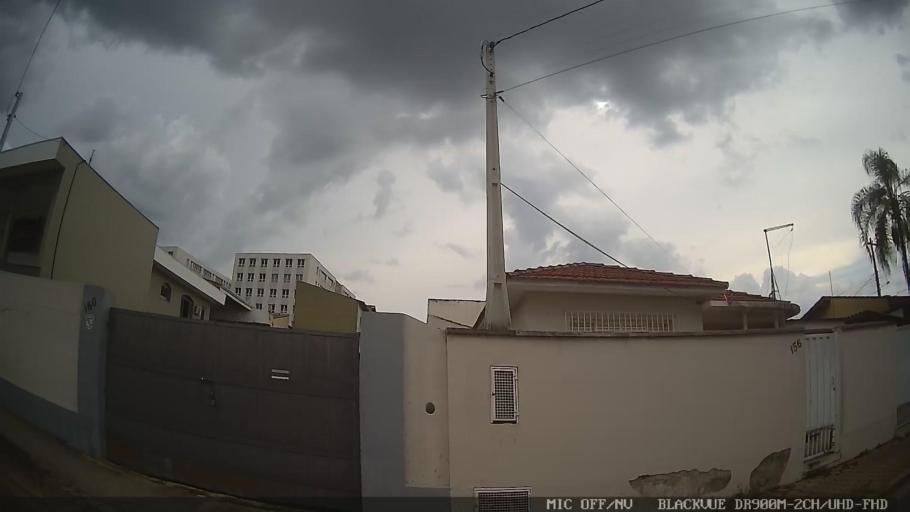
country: BR
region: Sao Paulo
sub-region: Atibaia
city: Atibaia
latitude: -23.1172
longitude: -46.5648
